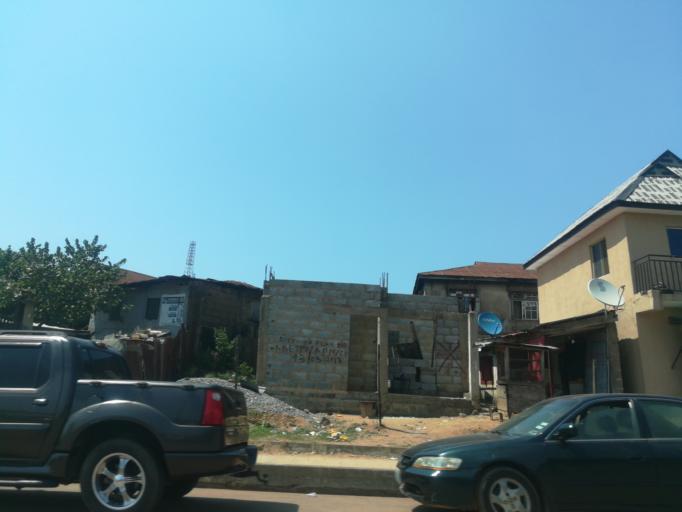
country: NG
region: Ogun
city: Abeokuta
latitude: 7.1669
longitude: 3.3577
